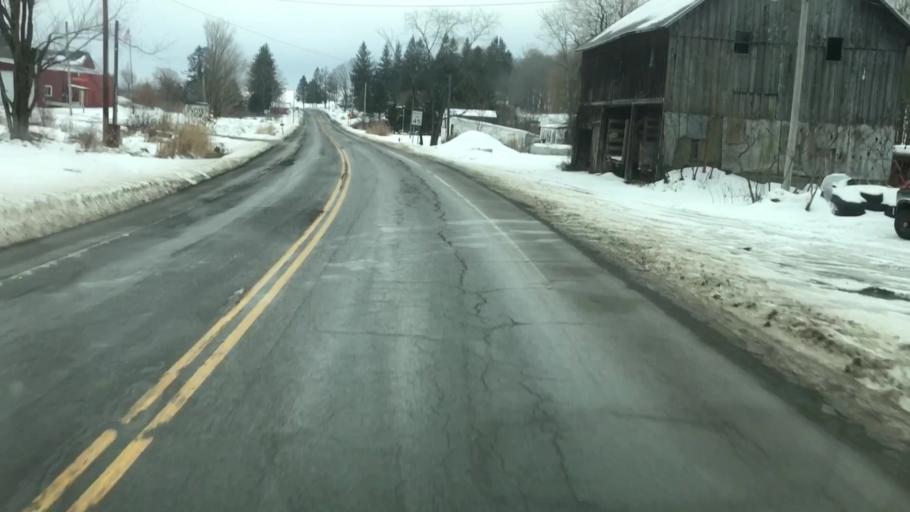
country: US
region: New York
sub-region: Cayuga County
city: Moravia
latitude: 42.7294
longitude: -76.3152
